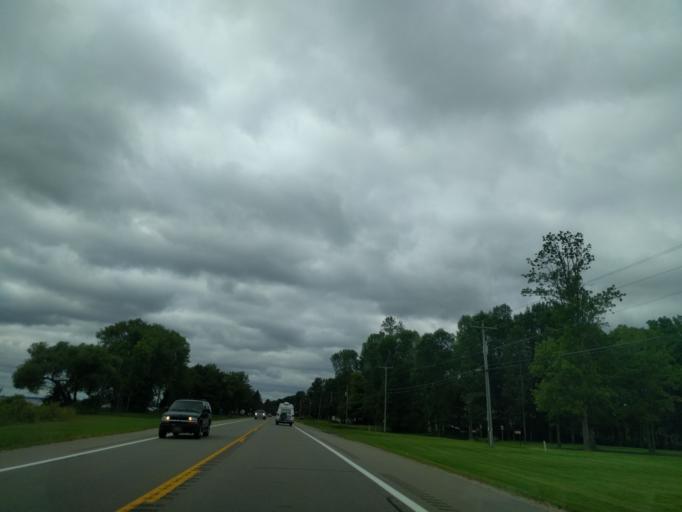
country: US
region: Michigan
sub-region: Menominee County
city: Menominee
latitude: 45.1937
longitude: -87.5455
